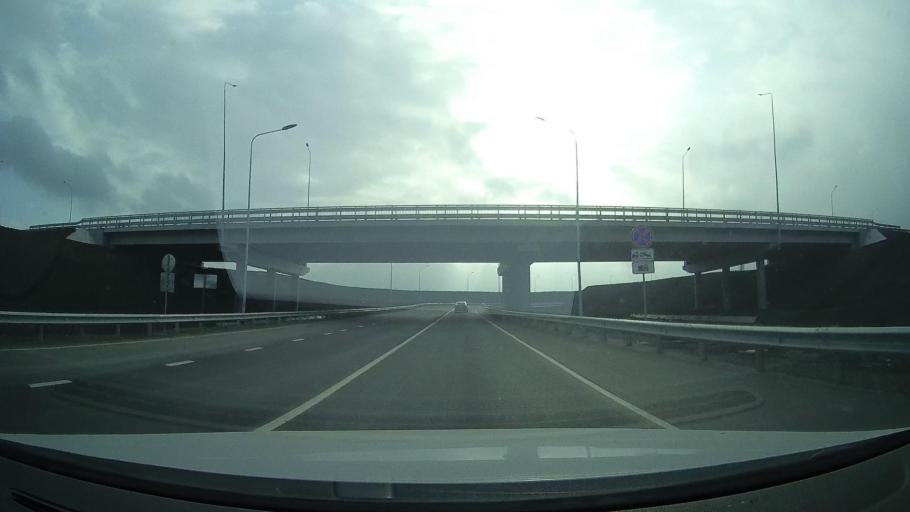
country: RU
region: Rostov
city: Grushevskaya
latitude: 47.3791
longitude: 39.8454
